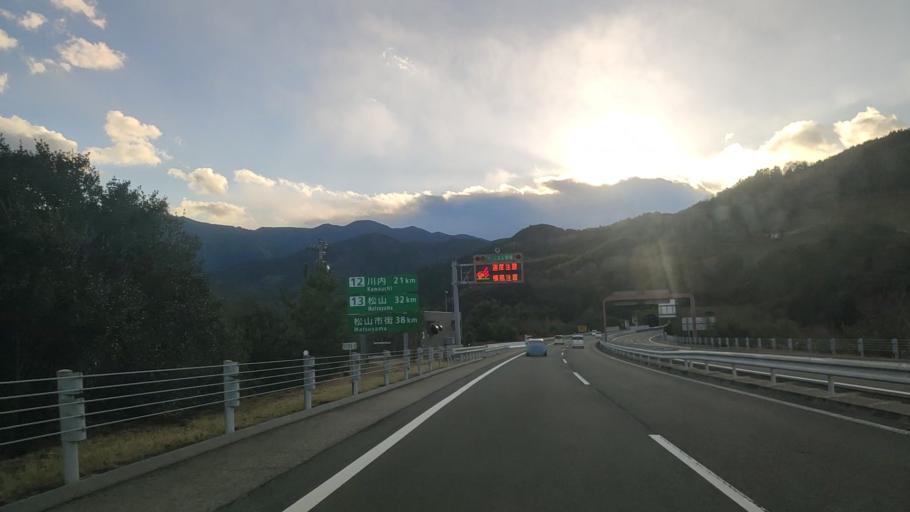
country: JP
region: Ehime
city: Saijo
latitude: 33.8777
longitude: 133.0822
